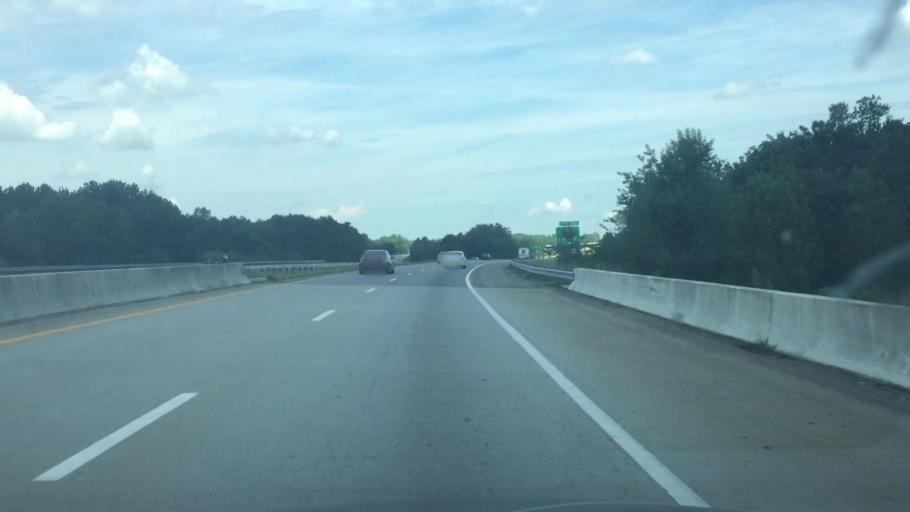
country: US
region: North Carolina
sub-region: Richmond County
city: Hamlet
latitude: 34.8542
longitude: -79.7374
